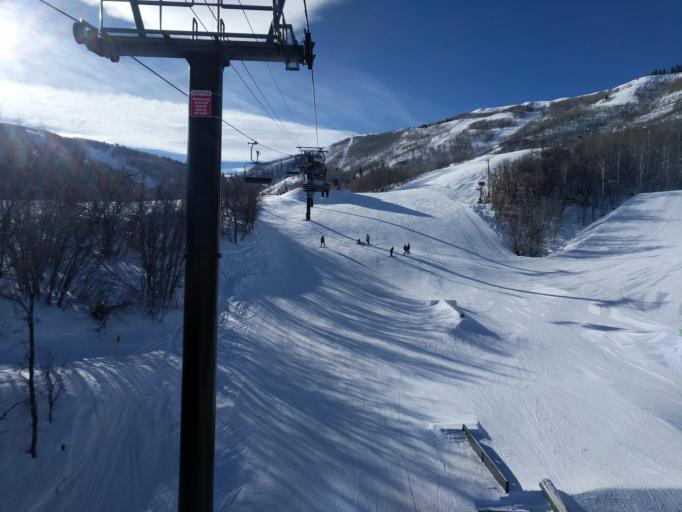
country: US
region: Utah
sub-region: Summit County
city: Park City
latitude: 40.6501
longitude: -111.5107
